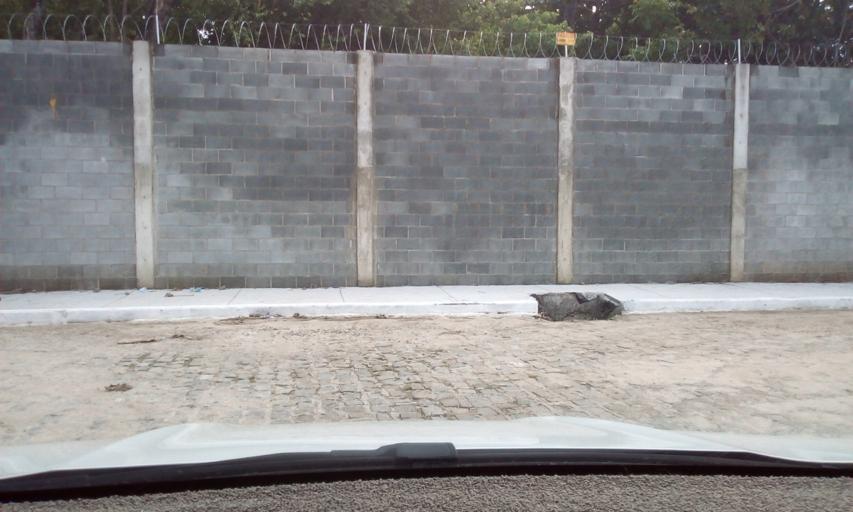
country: BR
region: Paraiba
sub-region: Bayeux
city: Bayeux
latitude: -7.1683
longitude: -34.8914
